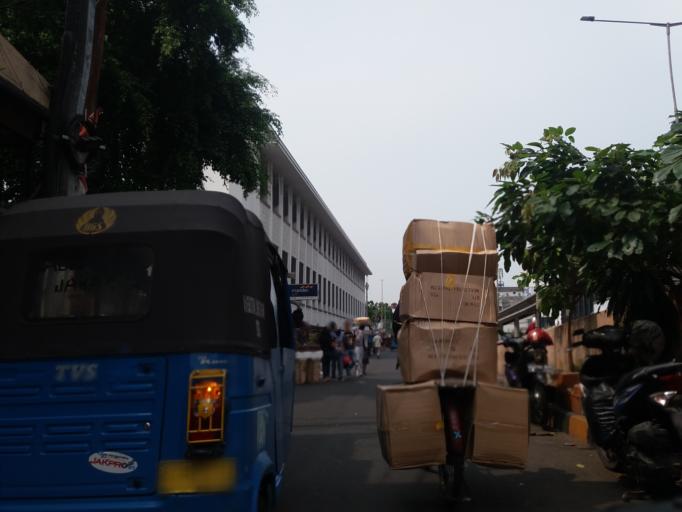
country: ID
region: Jakarta Raya
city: Jakarta
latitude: -6.1388
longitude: 106.8127
